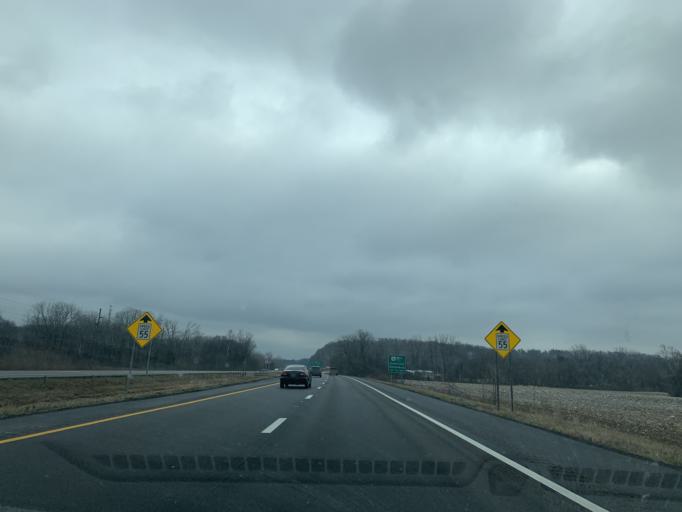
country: US
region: Ohio
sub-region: Licking County
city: Granville South
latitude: 40.0637
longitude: -82.5378
